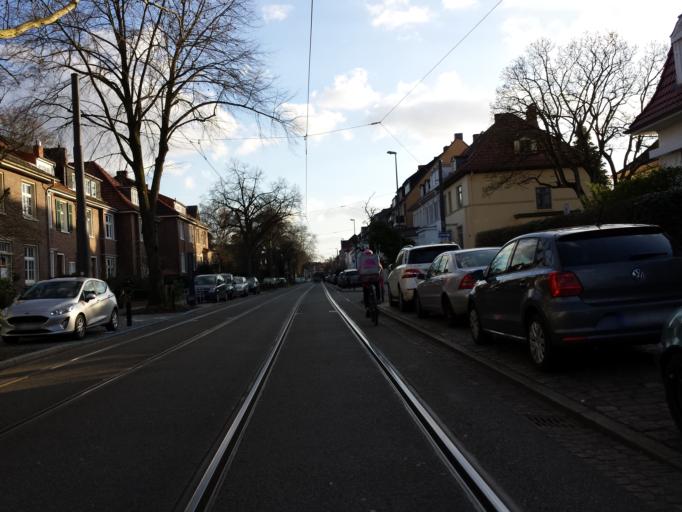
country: DE
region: Bremen
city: Bremen
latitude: 53.0909
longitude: 8.8347
